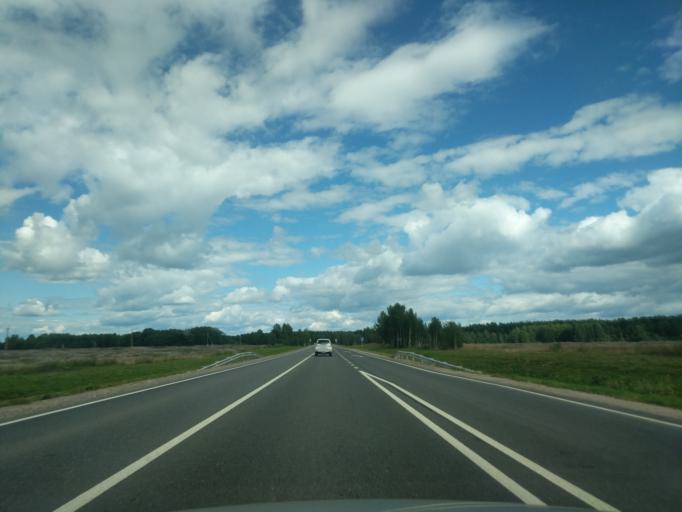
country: RU
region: Kostroma
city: Oktyabr'skiy
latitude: 57.7873
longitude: 41.1278
